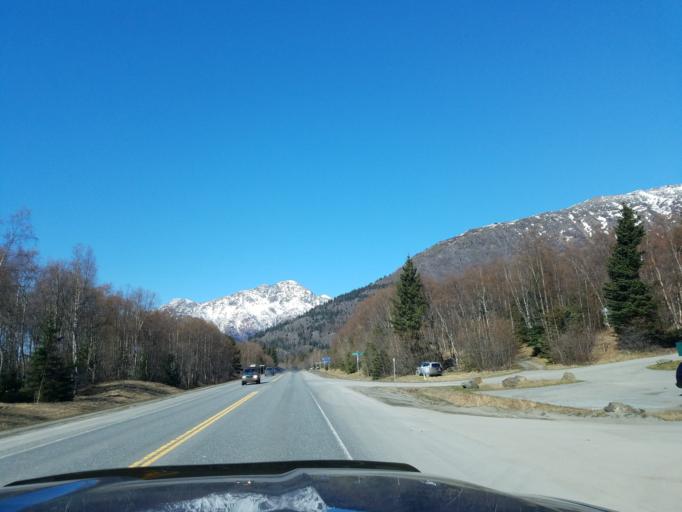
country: US
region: Alaska
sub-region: Anchorage Municipality
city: Girdwood
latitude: 60.9671
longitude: -149.4440
